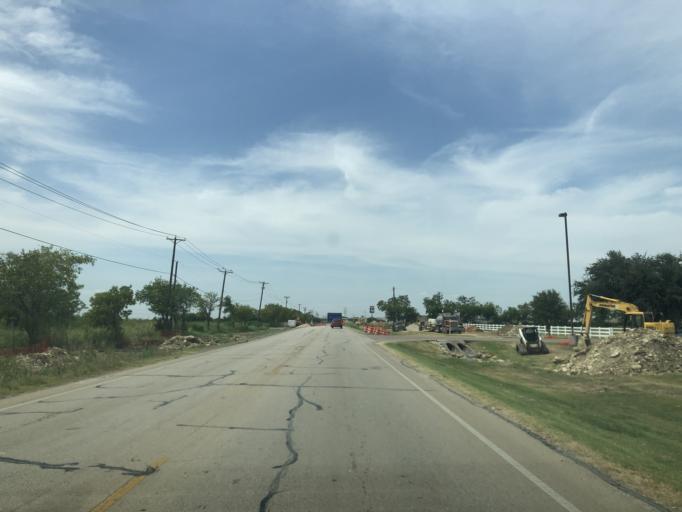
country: US
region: Texas
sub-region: Tarrant County
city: Saginaw
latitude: 32.9084
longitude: -97.3489
